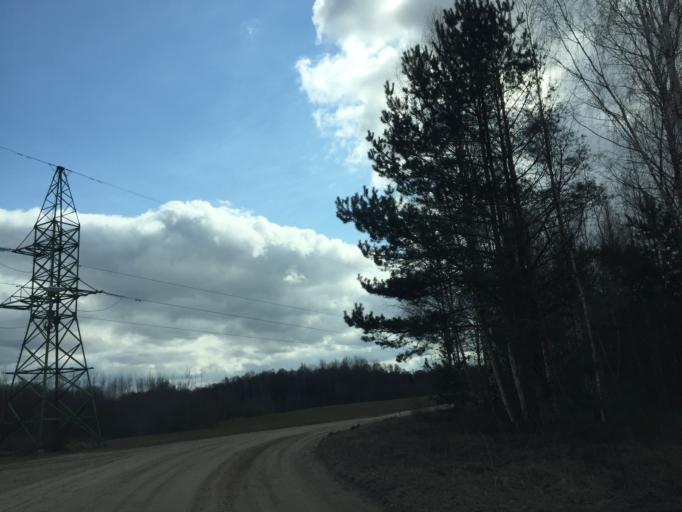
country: LV
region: Vecumnieki
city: Vecumnieki
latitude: 56.5839
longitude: 24.6060
